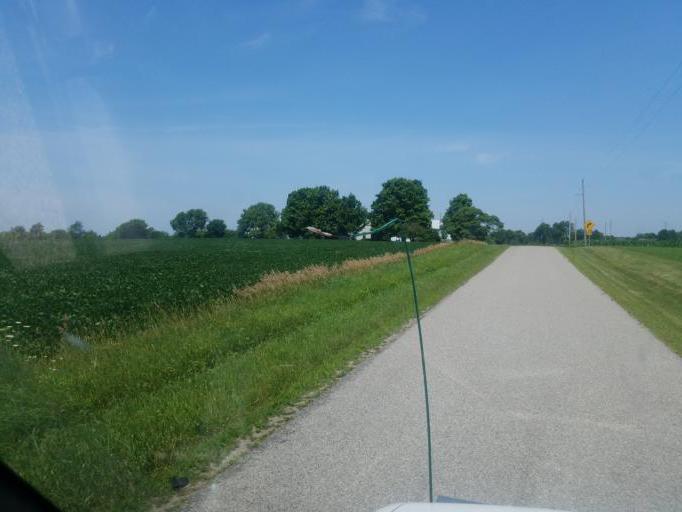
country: US
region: Ohio
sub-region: Logan County
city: West Liberty
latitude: 40.2838
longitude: -83.7700
